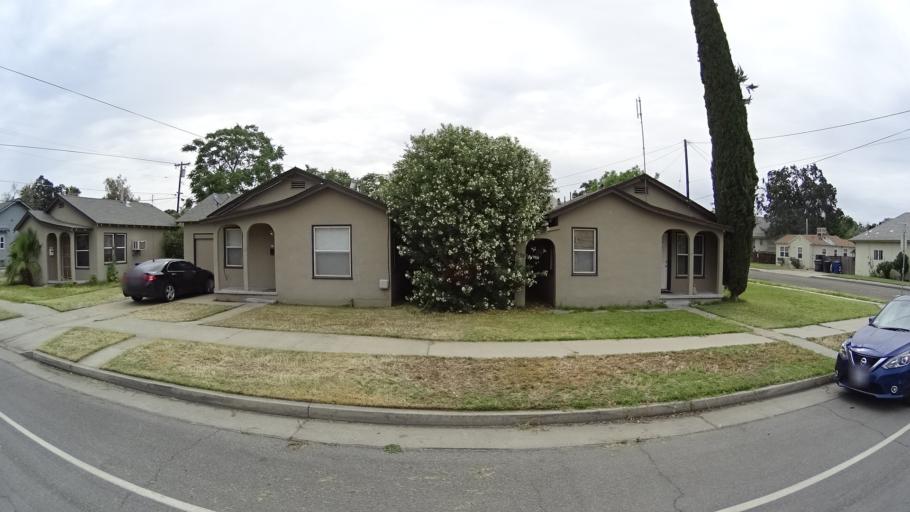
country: US
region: California
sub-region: Kings County
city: Hanford
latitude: 36.3387
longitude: -119.6493
